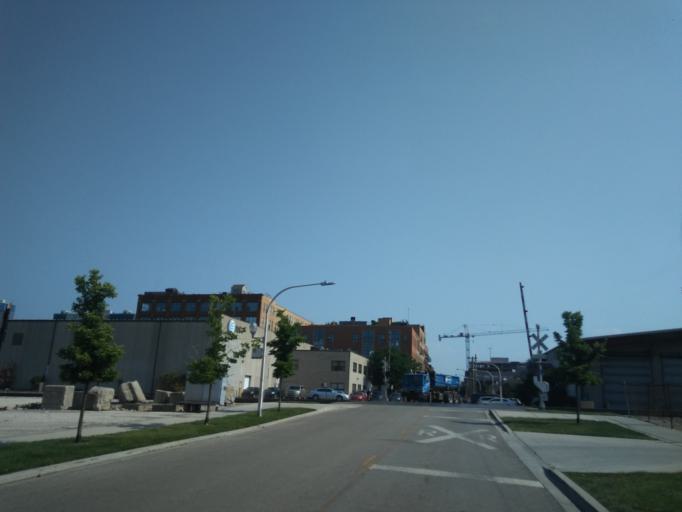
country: US
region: Illinois
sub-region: Cook County
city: Chicago
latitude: 41.8888
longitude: -87.6569
